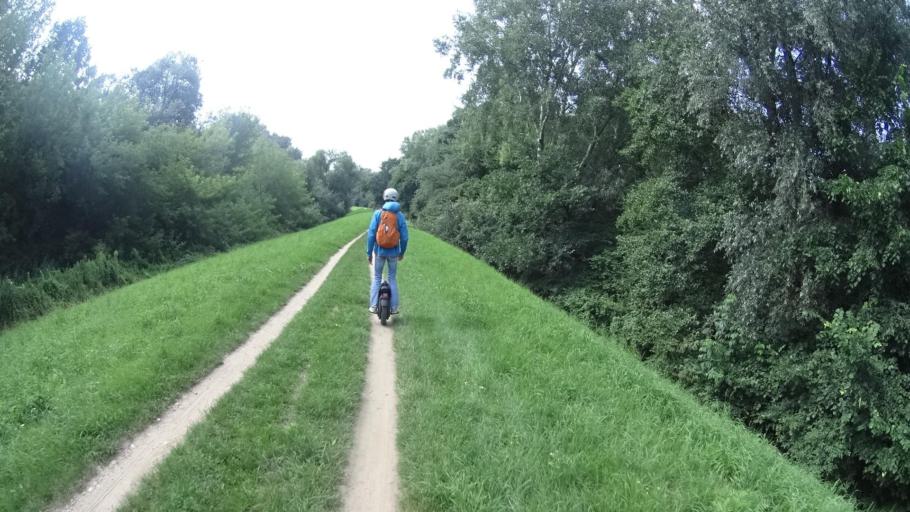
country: PL
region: Masovian Voivodeship
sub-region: Powiat legionowski
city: Jablonna
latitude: 52.3708
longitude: 20.9141
